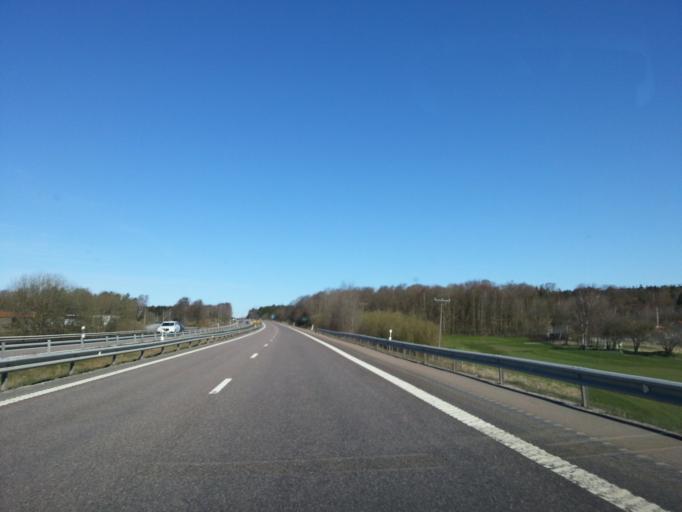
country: SE
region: Vaestra Goetaland
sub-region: Kungalvs Kommun
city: Kode
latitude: 57.9344
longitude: 11.8703
